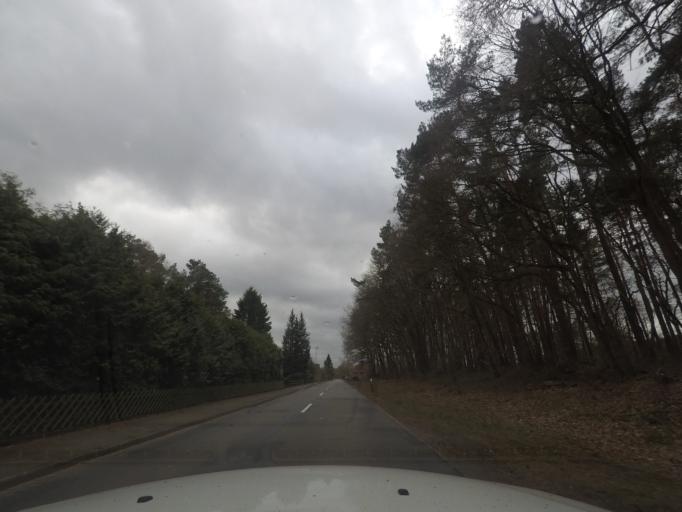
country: DE
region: Lower Saxony
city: Bad Bevensen
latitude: 53.0507
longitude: 10.6062
